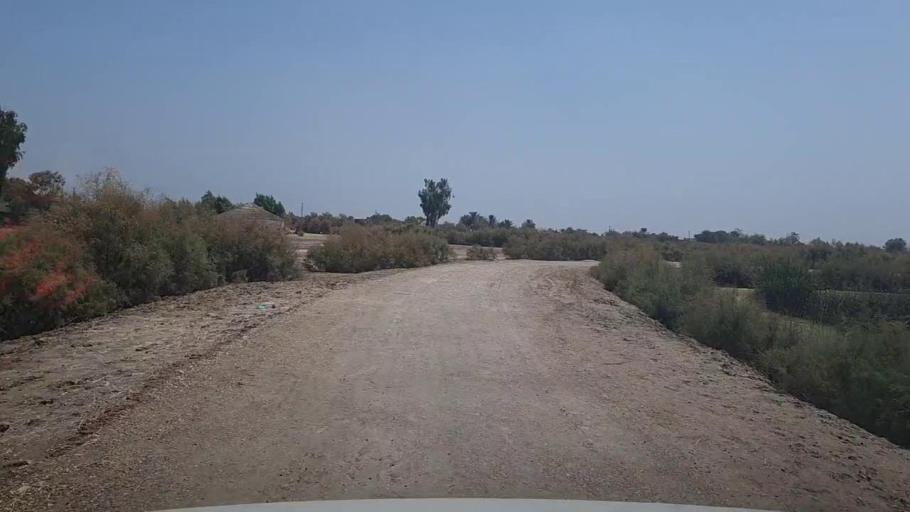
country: PK
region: Sindh
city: Kandhkot
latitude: 28.3088
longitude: 69.3569
